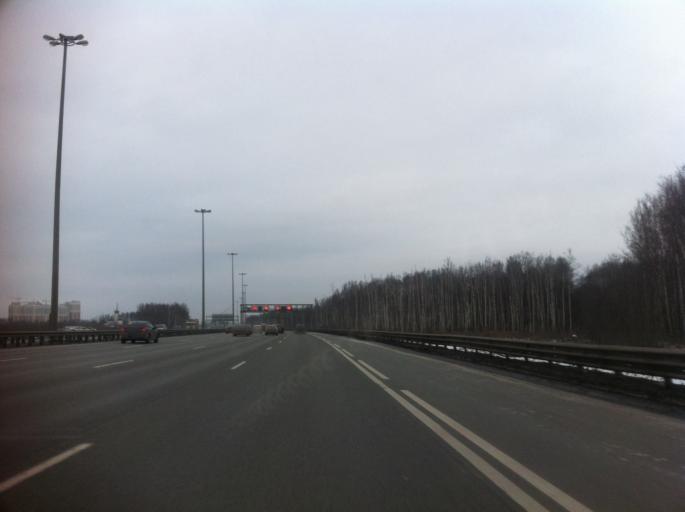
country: RU
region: Leningrad
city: Rybatskoye
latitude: 59.8906
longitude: 30.5242
